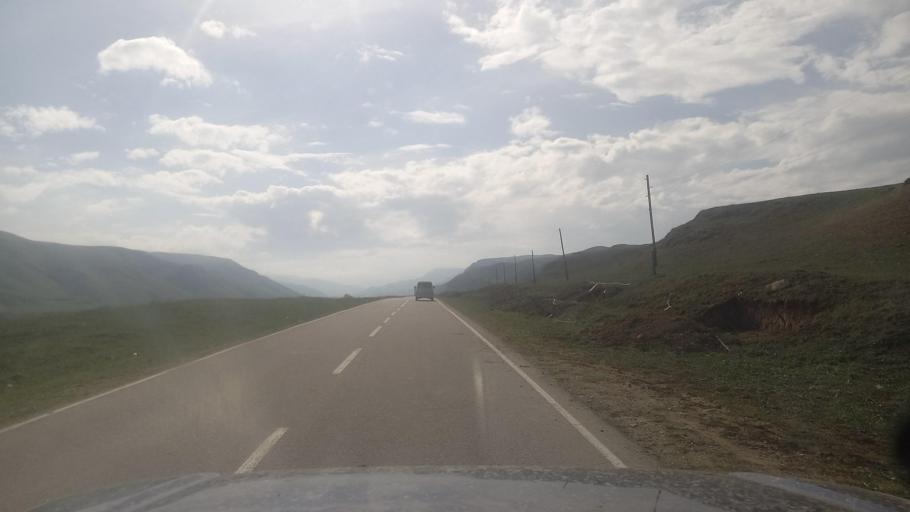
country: RU
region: Kabardino-Balkariya
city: Kamennomostskoye
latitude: 43.7358
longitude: 42.9963
